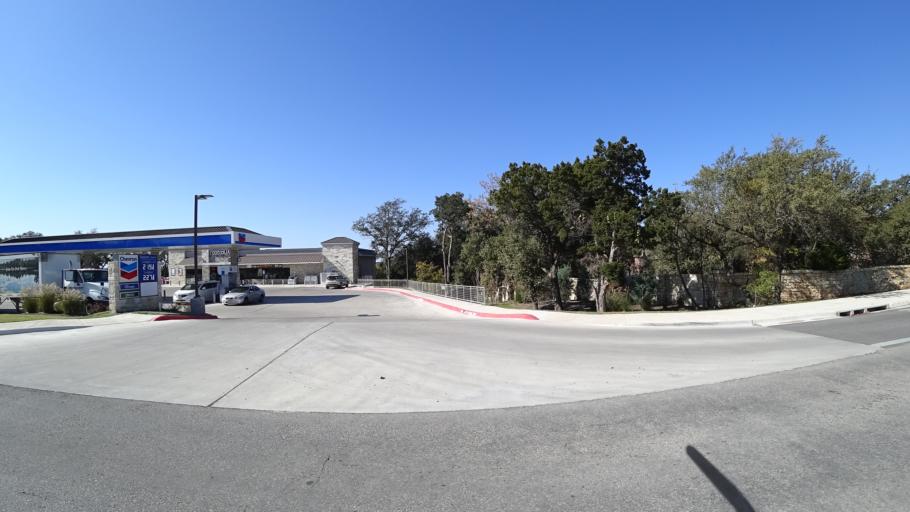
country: US
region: Texas
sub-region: Williamson County
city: Anderson Mill
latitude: 30.4669
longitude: -97.8440
